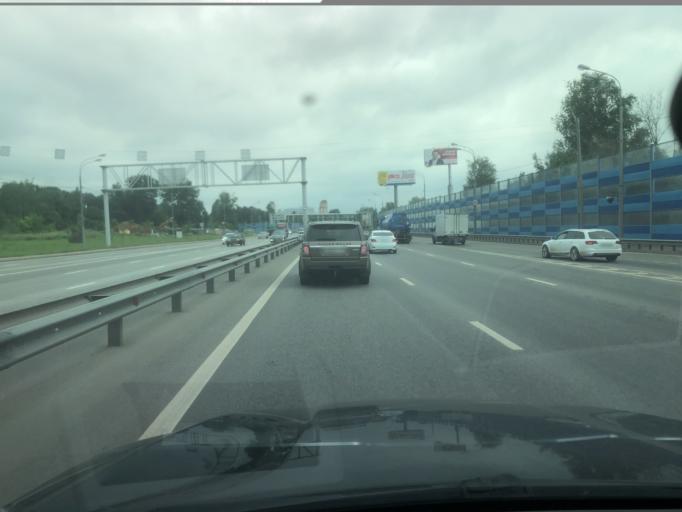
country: RU
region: Moscow
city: Severnyy
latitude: 55.9460
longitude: 37.5417
